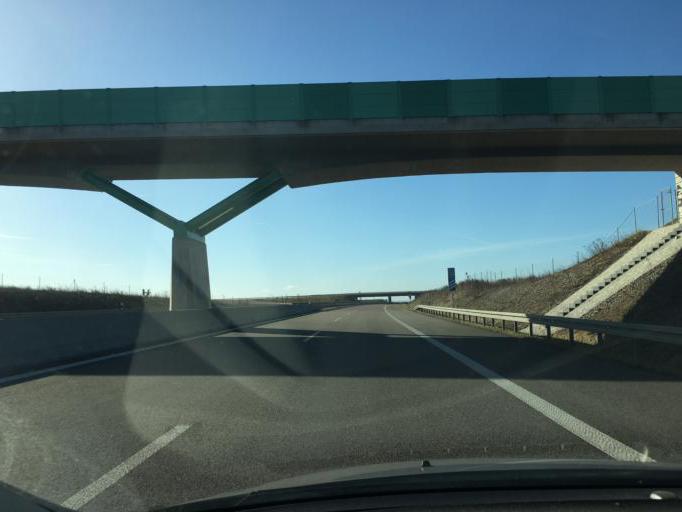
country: DE
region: Saxony
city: Narsdorf
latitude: 50.9995
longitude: 12.6901
